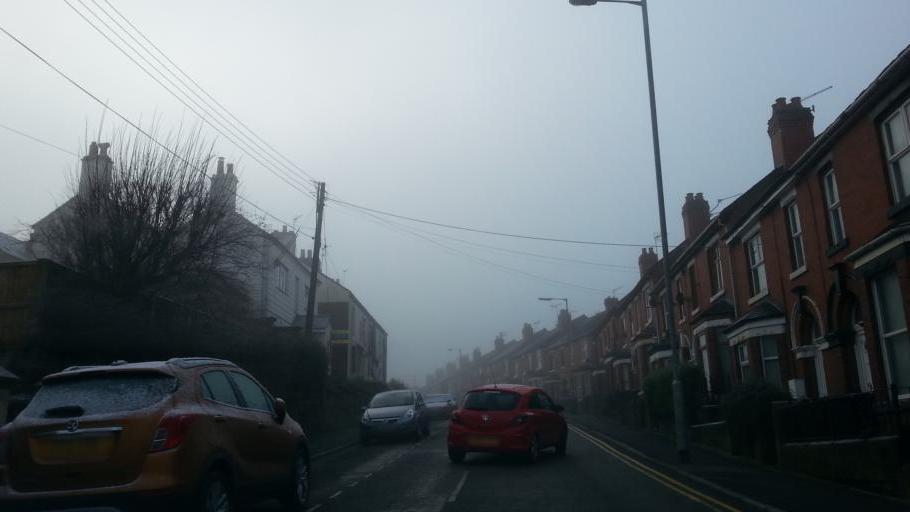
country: GB
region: England
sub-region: Staffordshire
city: Biddulph
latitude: 53.1137
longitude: -2.1773
